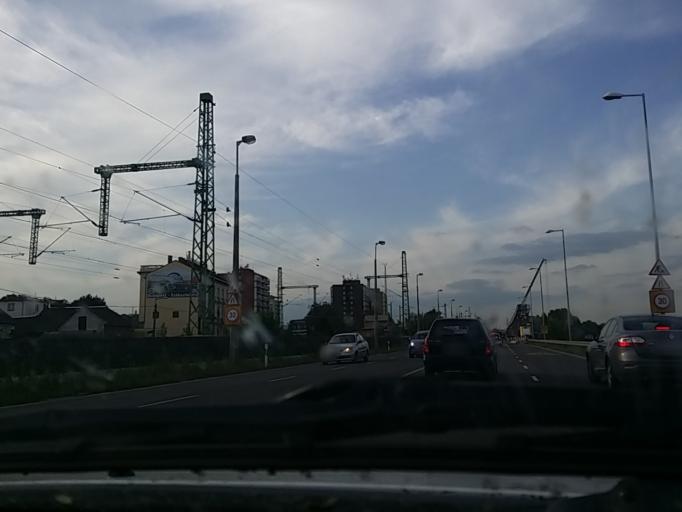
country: HU
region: Budapest
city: Budapest XXII. keruelet
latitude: 47.4217
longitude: 19.0421
